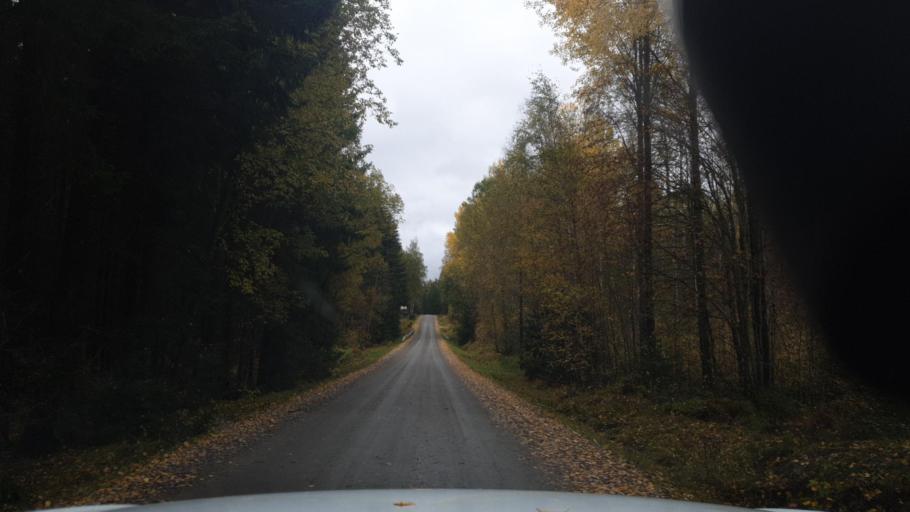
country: SE
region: Vaermland
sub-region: Karlstads Kommun
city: Edsvalla
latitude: 59.5044
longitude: 13.1990
